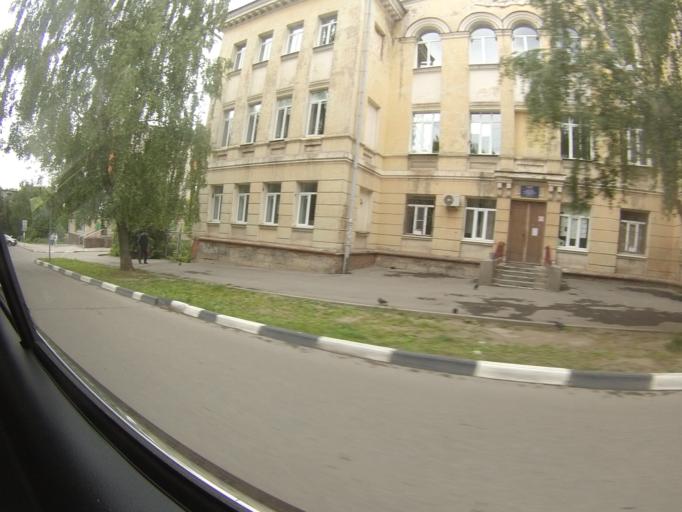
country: RU
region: Tula
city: Tula
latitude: 54.1898
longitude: 37.5983
